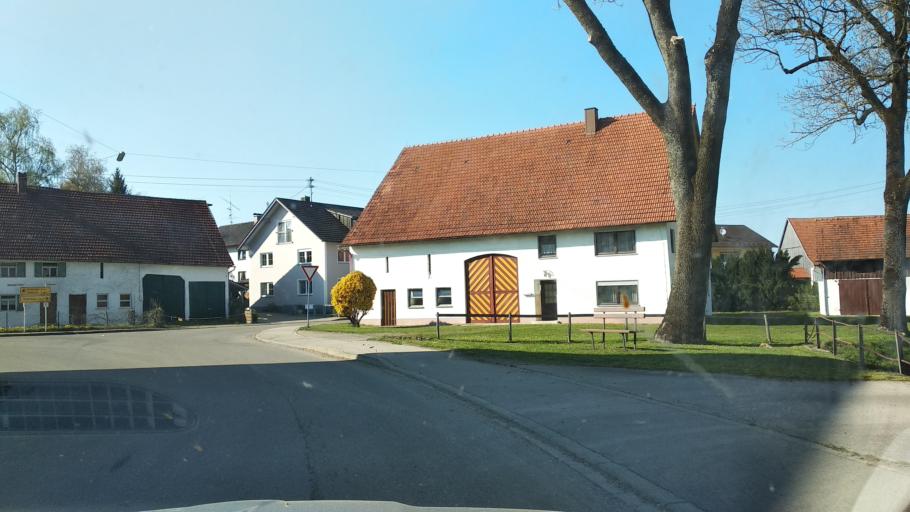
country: DE
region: Bavaria
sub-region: Swabia
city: Hawangen
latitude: 47.9709
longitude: 10.2633
